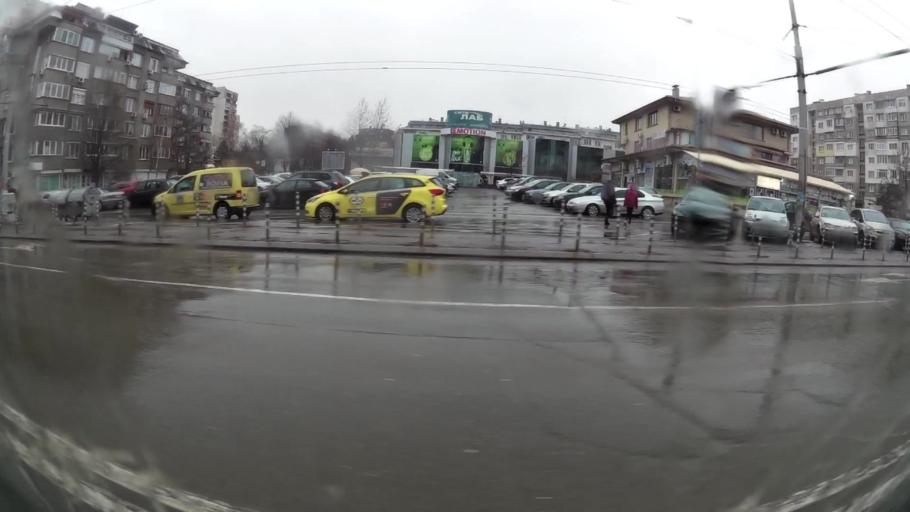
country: BG
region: Sofia-Capital
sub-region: Stolichna Obshtina
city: Sofia
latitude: 42.6559
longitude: 23.3752
